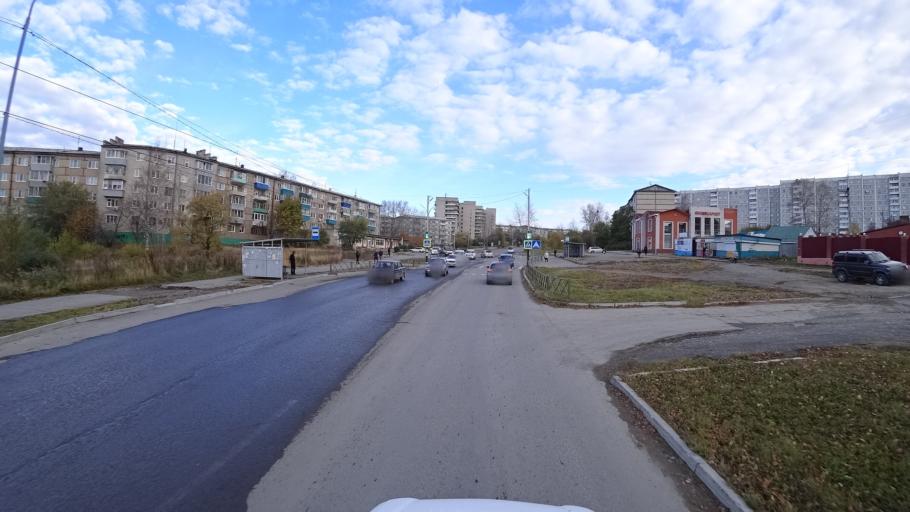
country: RU
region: Khabarovsk Krai
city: Amursk
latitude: 50.2370
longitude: 136.9110
